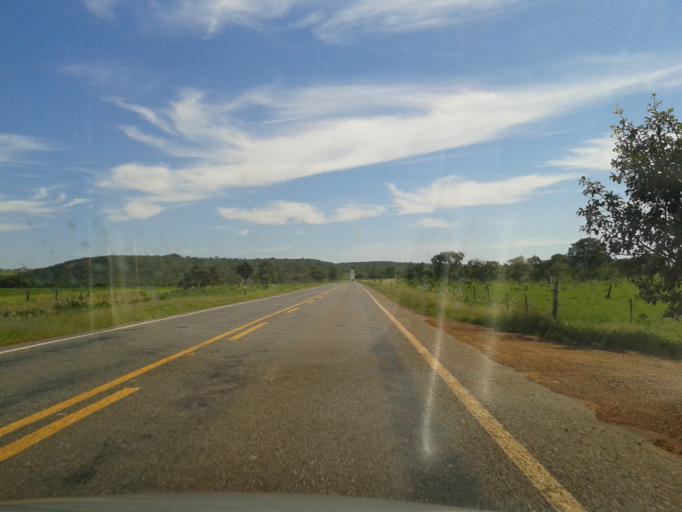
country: BR
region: Goias
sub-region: Piracanjuba
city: Piracanjuba
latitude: -17.2911
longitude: -48.7866
